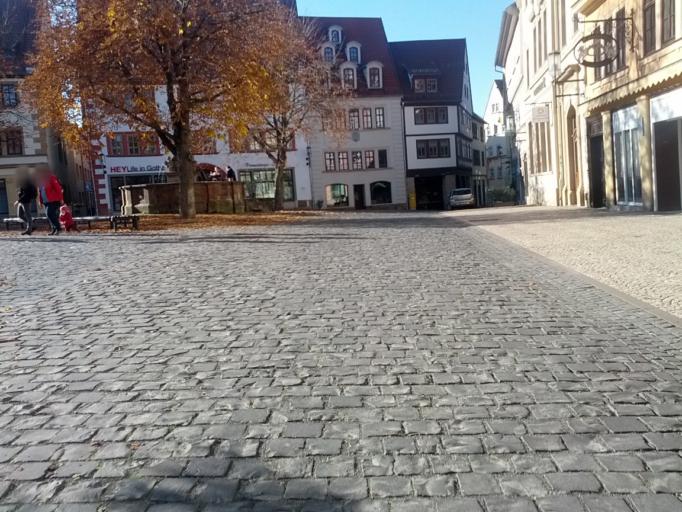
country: DE
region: Thuringia
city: Gotha
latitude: 50.9496
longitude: 10.7016
